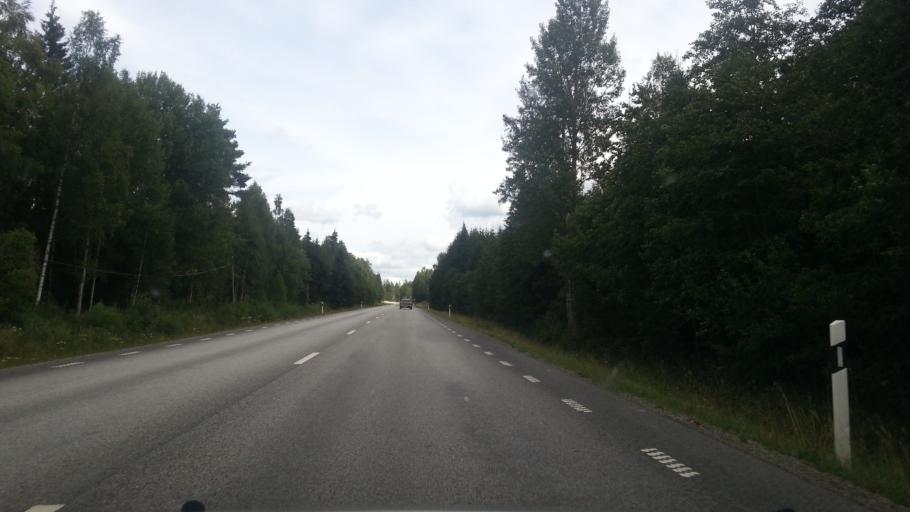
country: SE
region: OErebro
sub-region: Lindesbergs Kommun
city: Lindesberg
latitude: 59.6653
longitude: 15.2693
